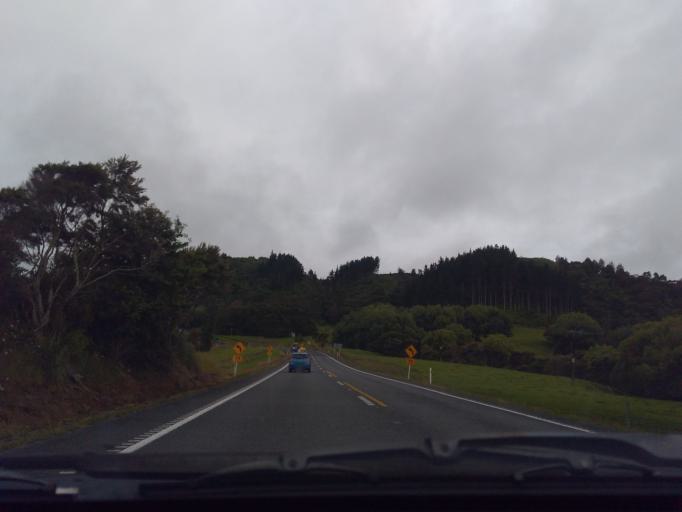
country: NZ
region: Northland
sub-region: Whangarei
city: Ruakaka
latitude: -36.1009
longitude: 174.4332
